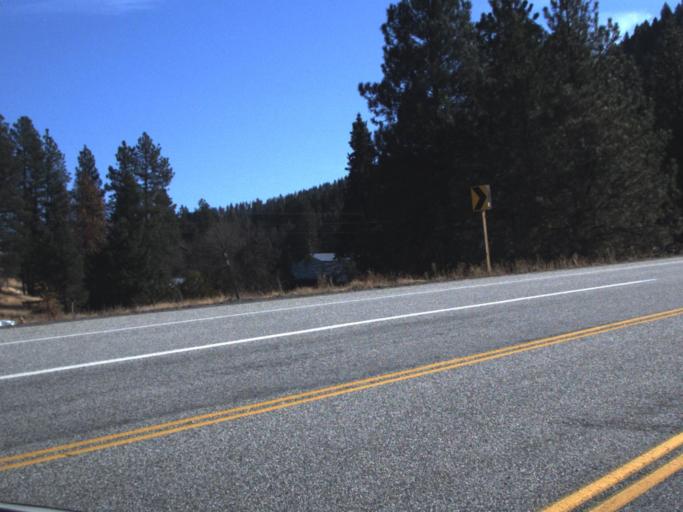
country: US
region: Washington
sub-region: Ferry County
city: Republic
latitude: 48.6502
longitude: -118.6844
